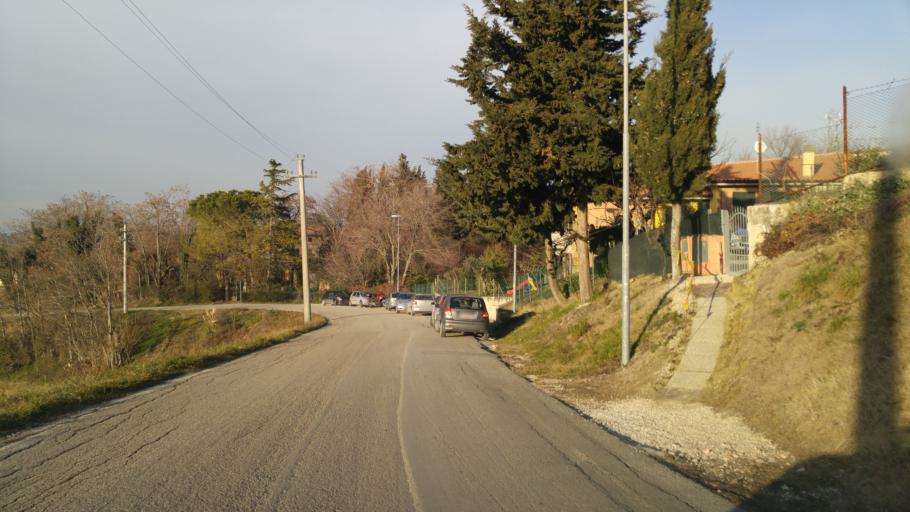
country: IT
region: The Marches
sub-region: Provincia di Pesaro e Urbino
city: Piagge
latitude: 43.7317
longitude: 12.9667
